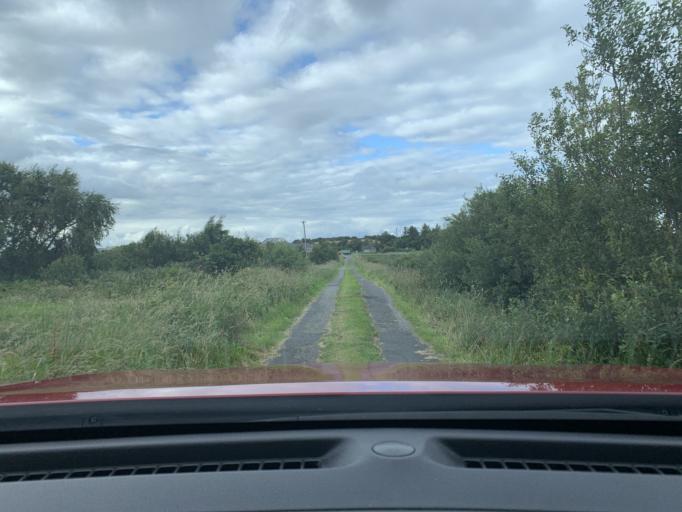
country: IE
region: Connaught
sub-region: County Leitrim
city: Kinlough
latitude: 54.4615
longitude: -8.3542
